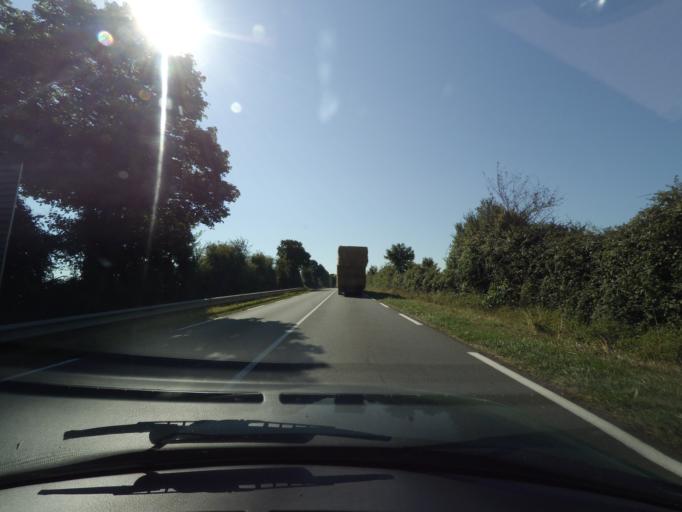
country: FR
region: Poitou-Charentes
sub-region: Departement de la Vienne
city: Lussac-les-Chateaux
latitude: 46.3940
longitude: 0.7348
